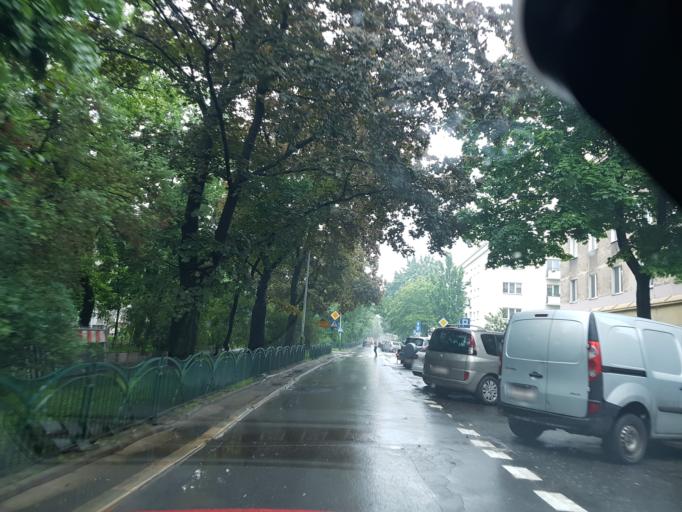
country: PL
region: Lesser Poland Voivodeship
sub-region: Krakow
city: Krakow
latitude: 50.0575
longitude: 19.9517
